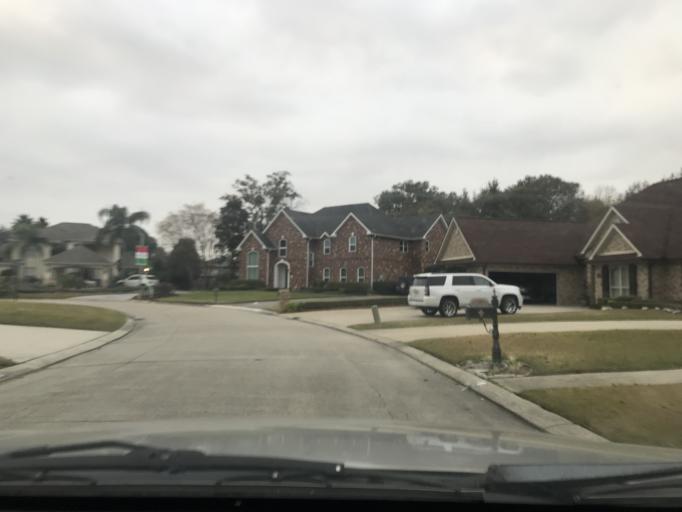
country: US
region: Louisiana
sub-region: Jefferson Parish
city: Woodmere
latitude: 29.8730
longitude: -90.0915
